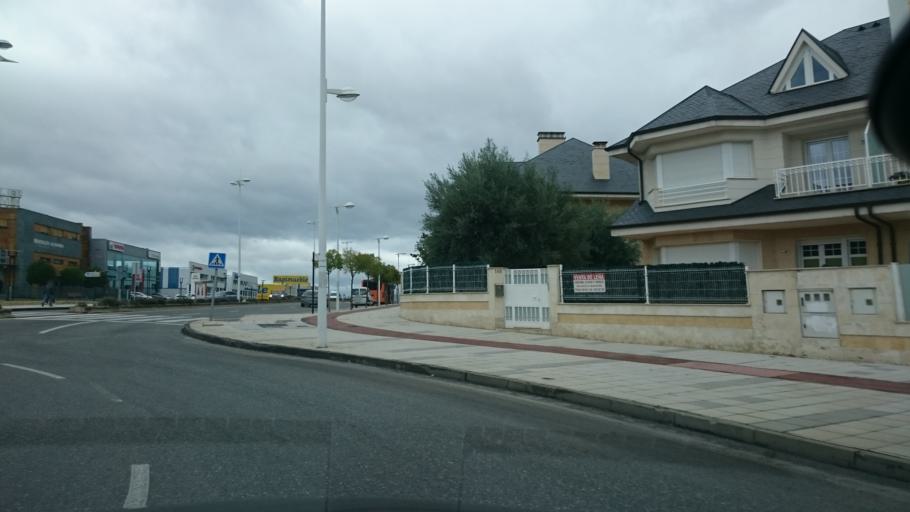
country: ES
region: Castille and Leon
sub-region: Provincia de Leon
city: Ponferrada
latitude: 42.5539
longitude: -6.6105
